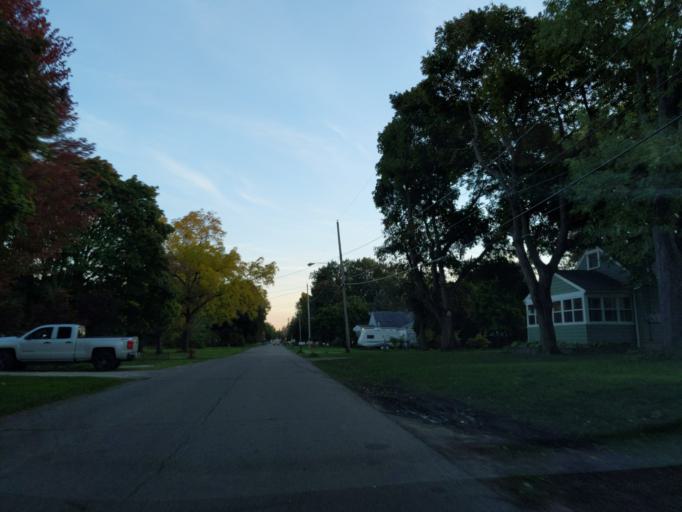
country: US
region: Michigan
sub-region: Ingham County
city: Edgemont Park
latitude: 42.7322
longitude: -84.5980
